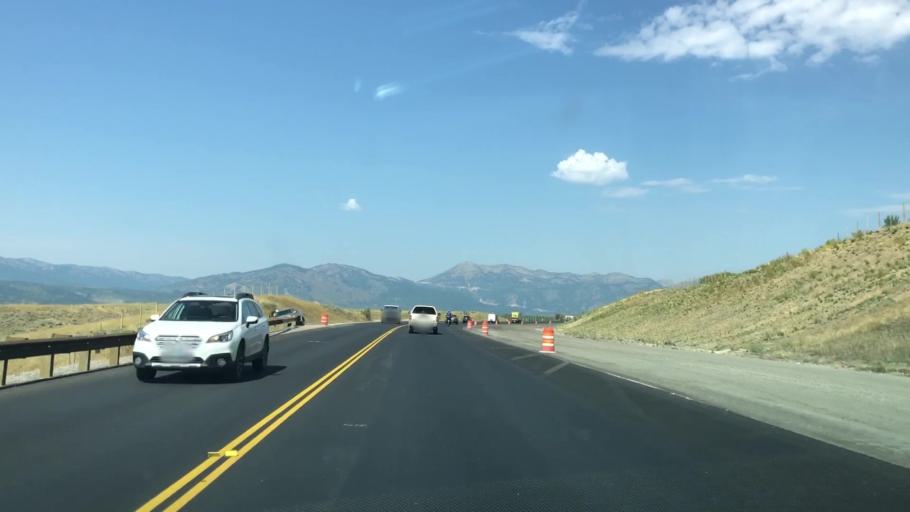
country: US
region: Wyoming
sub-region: Teton County
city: South Park
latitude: 43.4093
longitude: -110.7674
